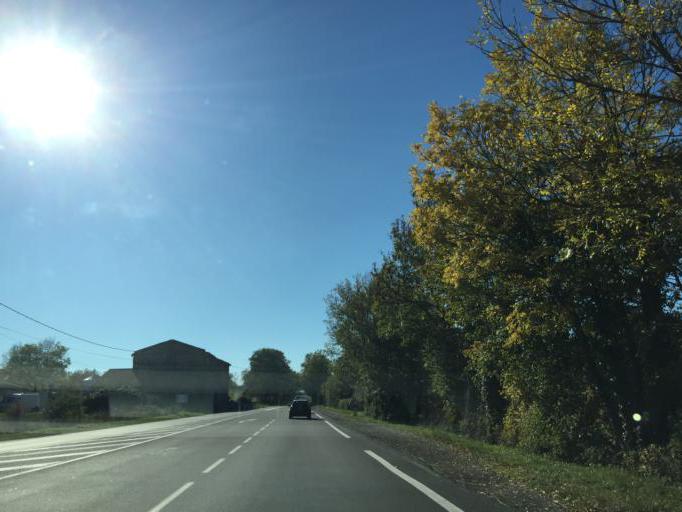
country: FR
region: Rhone-Alpes
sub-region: Departement du Rhone
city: Saint-Andeol-le-Chateau
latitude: 45.6035
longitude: 4.6875
